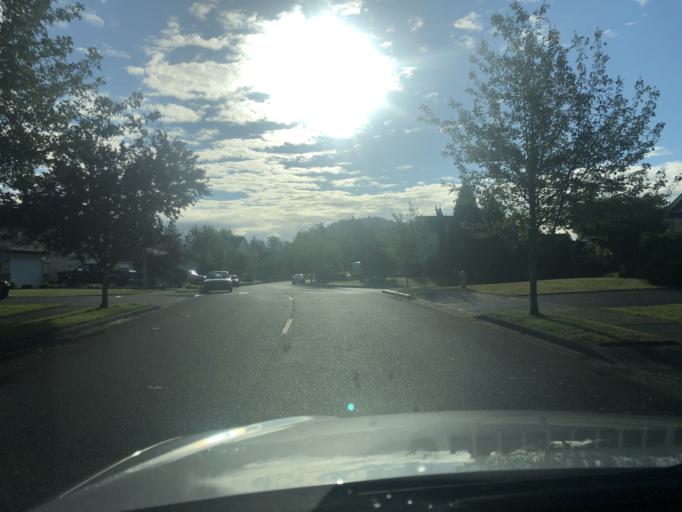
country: US
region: Washington
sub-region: Pierce County
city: Buckley
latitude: 47.1688
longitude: -122.0188
